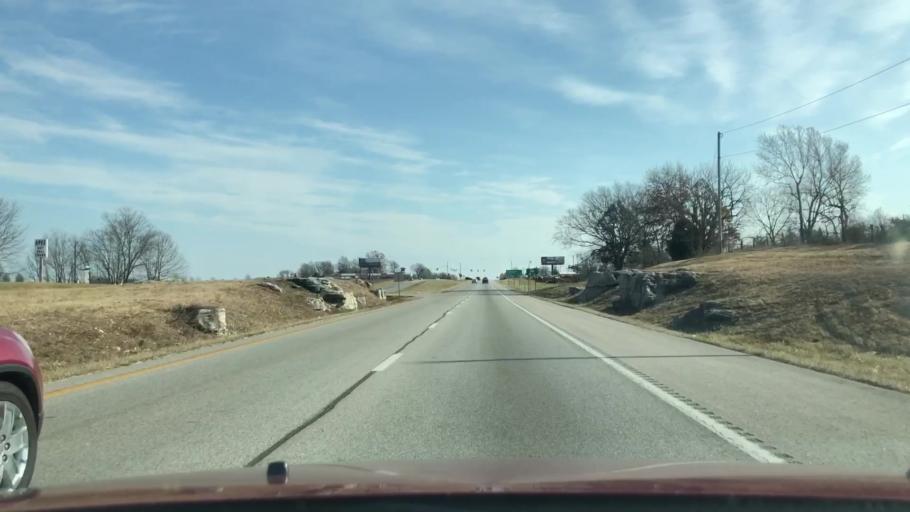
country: US
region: Missouri
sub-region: Webster County
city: Rogersville
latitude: 37.1188
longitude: -93.1250
